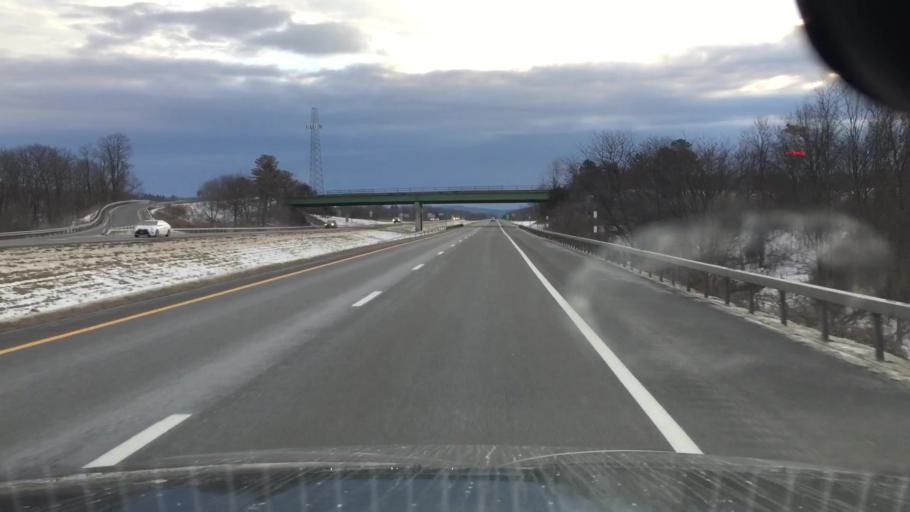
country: US
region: Pennsylvania
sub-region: Bradford County
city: South Waverly
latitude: 42.0007
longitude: -76.5897
